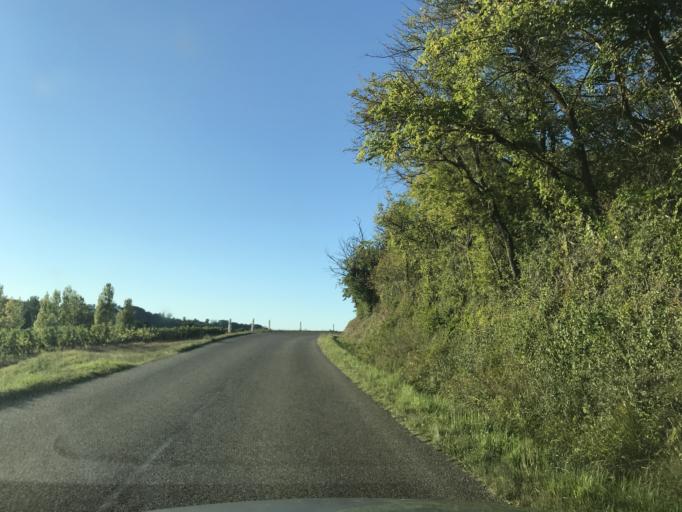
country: FR
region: Aquitaine
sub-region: Departement de la Gironde
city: Mouliets-et-Villemartin
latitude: 44.7963
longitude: -0.0439
